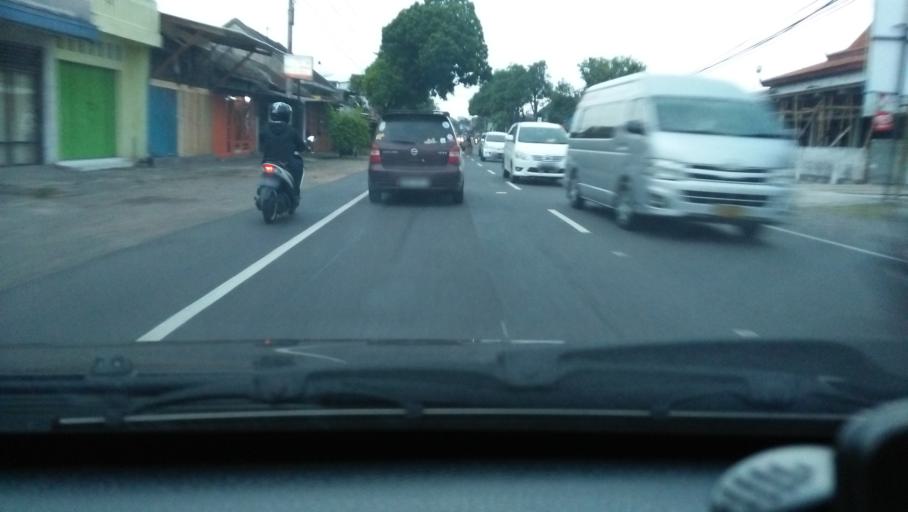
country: ID
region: Central Java
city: Magelang
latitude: -7.4253
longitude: 110.2308
